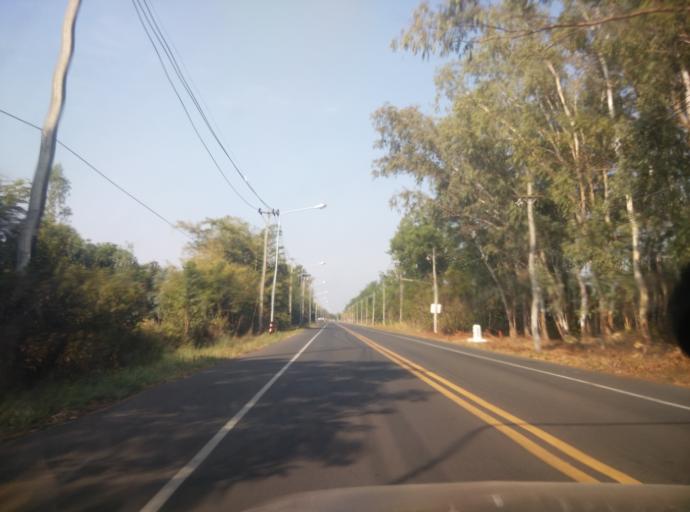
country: TH
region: Sisaket
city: Si Sa Ket
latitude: 15.1121
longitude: 104.2759
